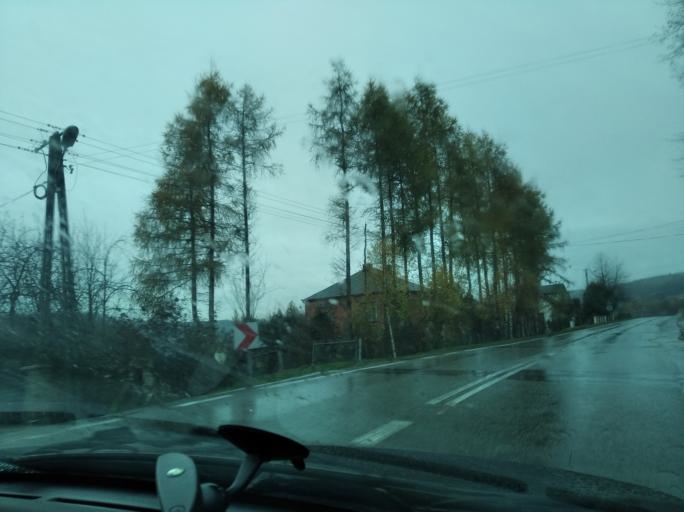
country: PL
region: Subcarpathian Voivodeship
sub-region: Powiat rzeszowski
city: Chmielnik
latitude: 49.9461
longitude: 22.1008
